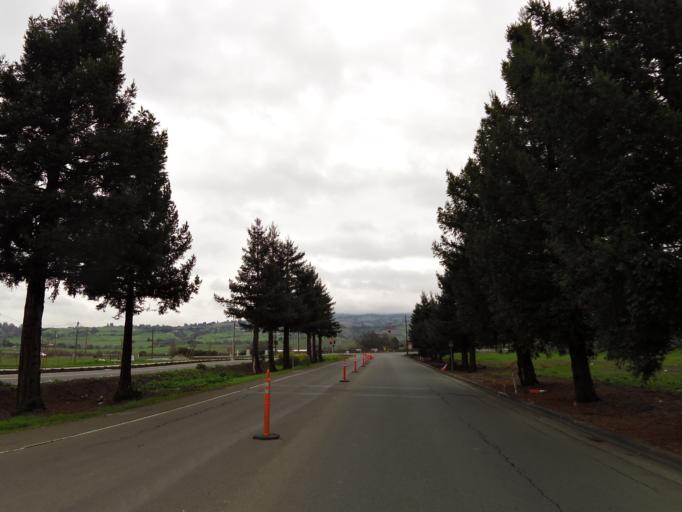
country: US
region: California
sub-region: Sonoma County
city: Rohnert Park
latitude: 38.3460
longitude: -122.6686
